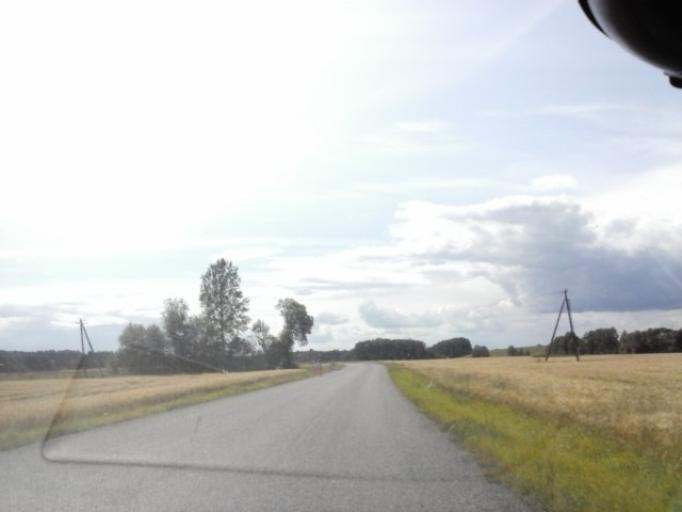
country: EE
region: Tartu
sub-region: UElenurme vald
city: Ulenurme
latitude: 58.2942
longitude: 26.9117
